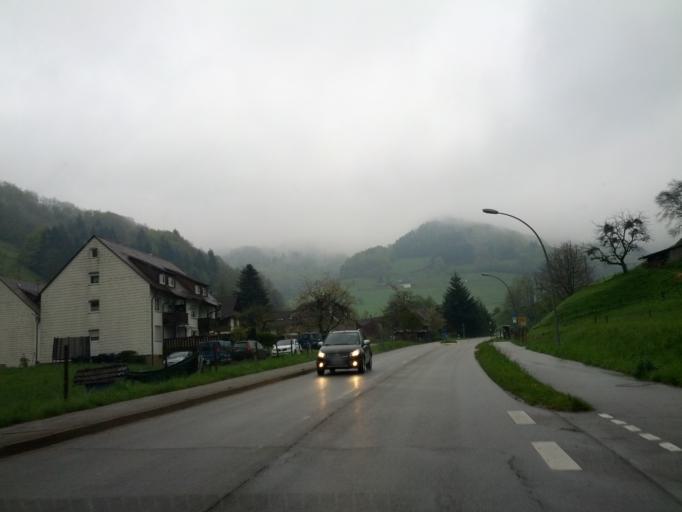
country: DE
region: Baden-Wuerttemberg
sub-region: Freiburg Region
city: Muenstertal/Schwarzwald
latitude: 47.8776
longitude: 7.8316
